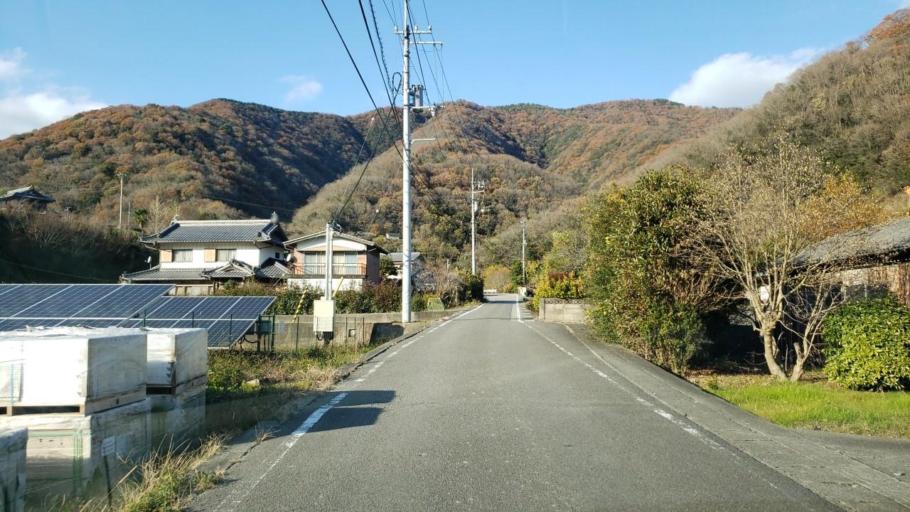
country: JP
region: Tokushima
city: Wakimachi
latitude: 34.0738
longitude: 134.0837
